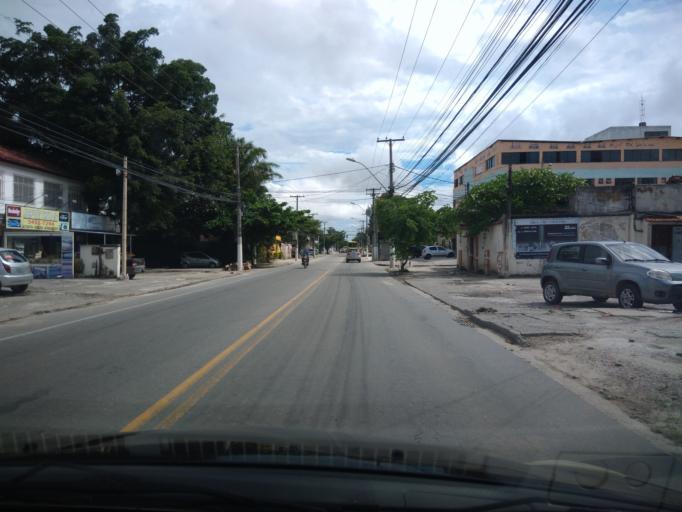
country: BR
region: Rio de Janeiro
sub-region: Niteroi
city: Niteroi
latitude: -22.9392
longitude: -43.0269
